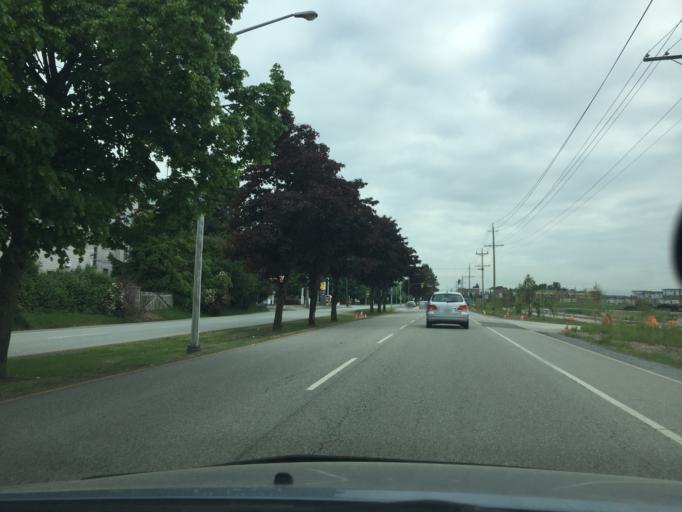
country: CA
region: British Columbia
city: Richmond
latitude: 49.1723
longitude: -123.1245
